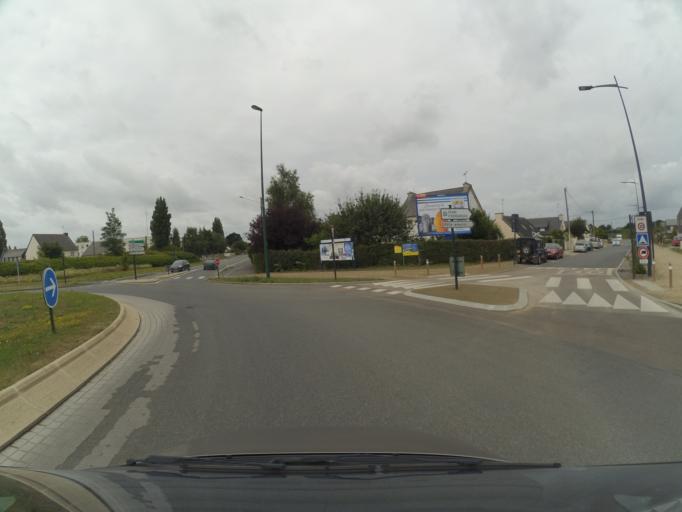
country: FR
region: Brittany
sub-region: Departement des Cotes-d'Armor
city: Ploufragan
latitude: 48.5181
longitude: -2.7995
